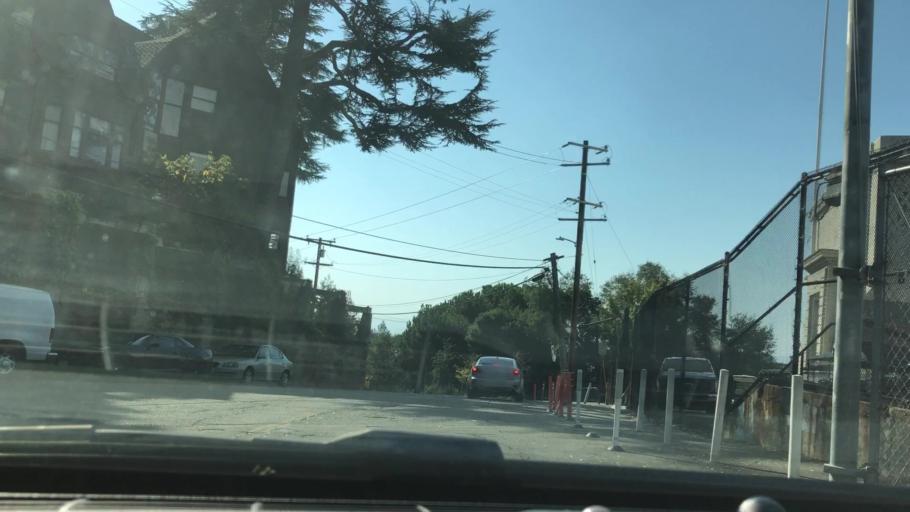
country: US
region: California
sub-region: Alameda County
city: Berkeley
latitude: 37.8704
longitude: -122.2495
